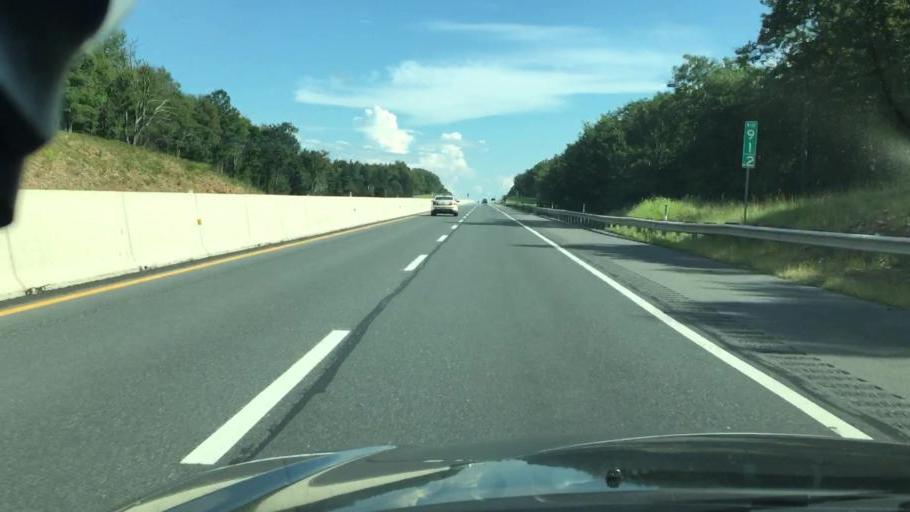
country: US
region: Pennsylvania
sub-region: Carbon County
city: Towamensing Trails
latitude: 41.0372
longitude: -75.6608
